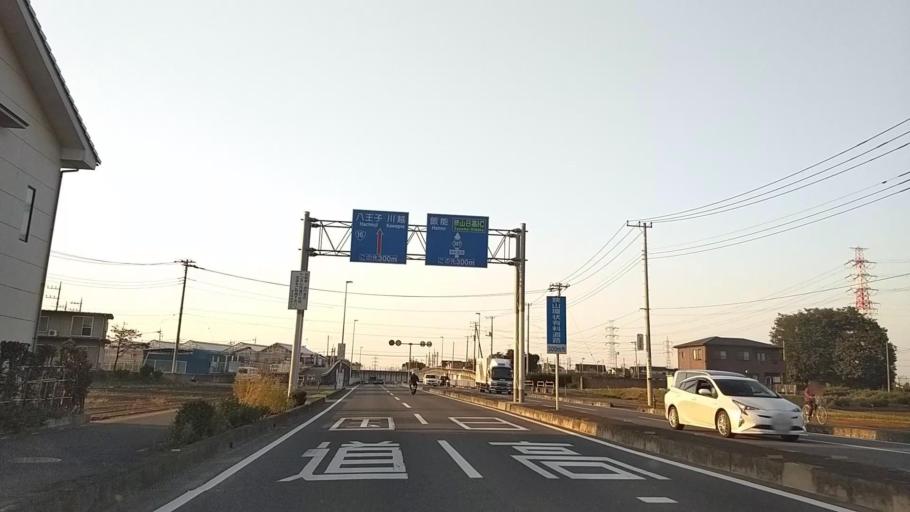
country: JP
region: Saitama
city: Sayama
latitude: 35.8649
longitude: 139.4258
